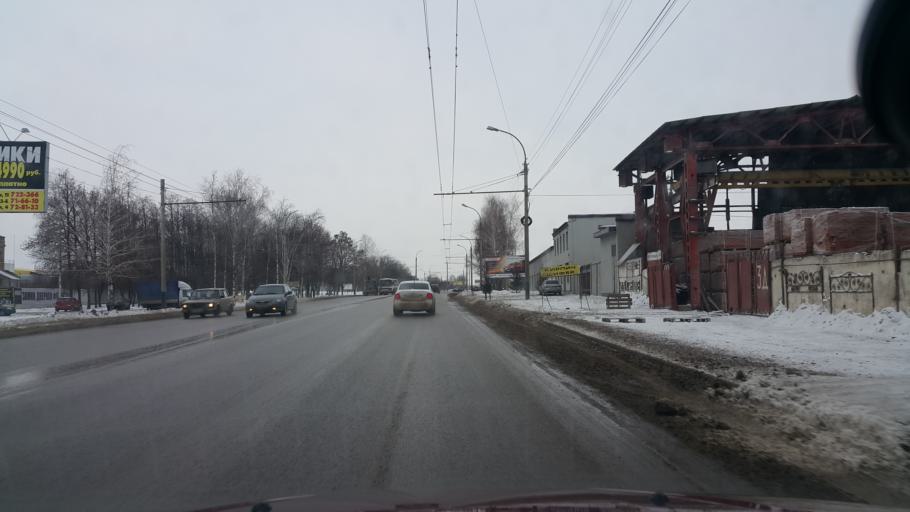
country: RU
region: Tambov
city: Tambov
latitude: 52.7346
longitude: 41.3940
